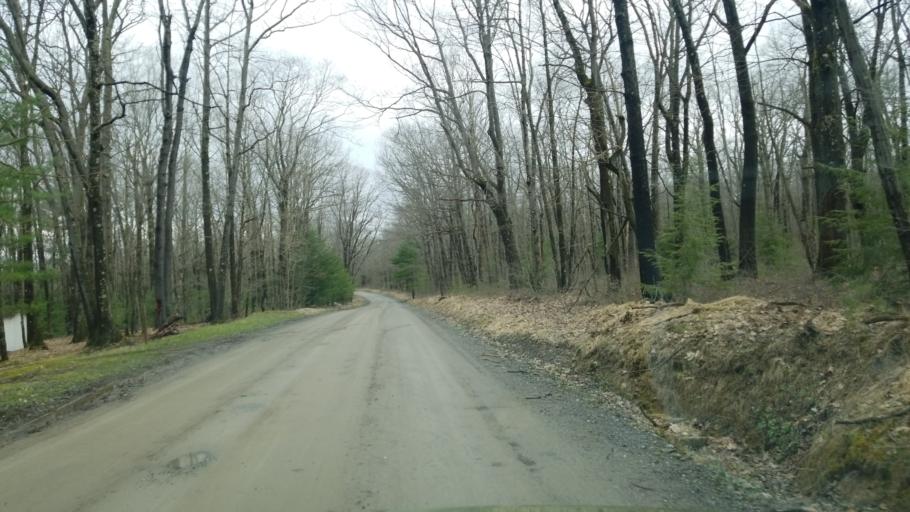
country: US
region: Pennsylvania
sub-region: Clearfield County
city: Shiloh
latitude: 41.1718
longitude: -78.3425
